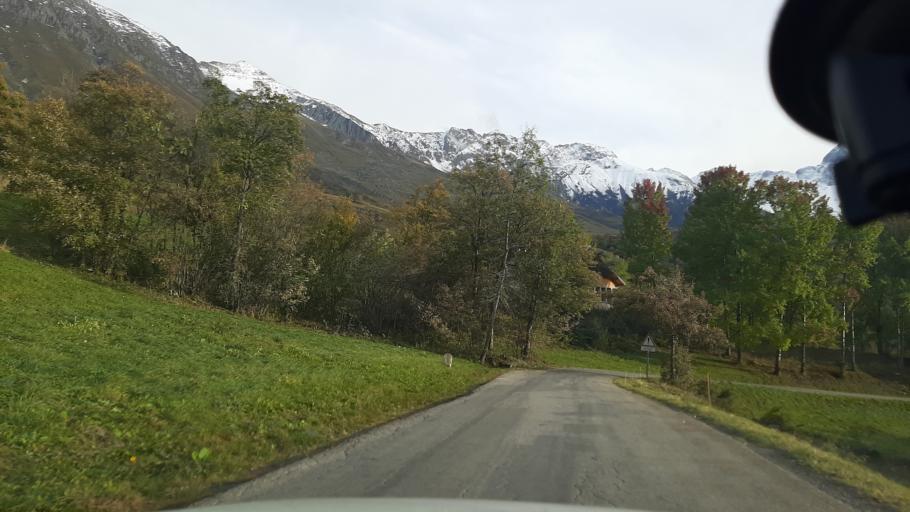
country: FR
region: Rhone-Alpes
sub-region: Departement de la Savoie
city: Villargondran
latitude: 45.2041
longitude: 6.3347
